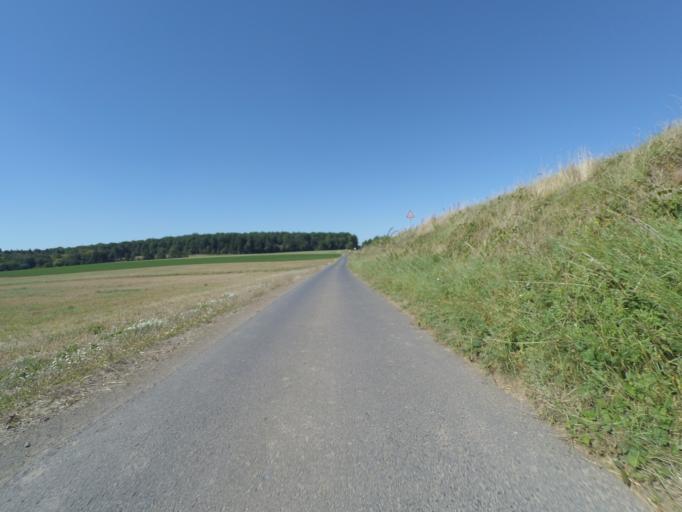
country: DE
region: Rheinland-Pfalz
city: Bad Bertrich
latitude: 50.0990
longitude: 7.0178
